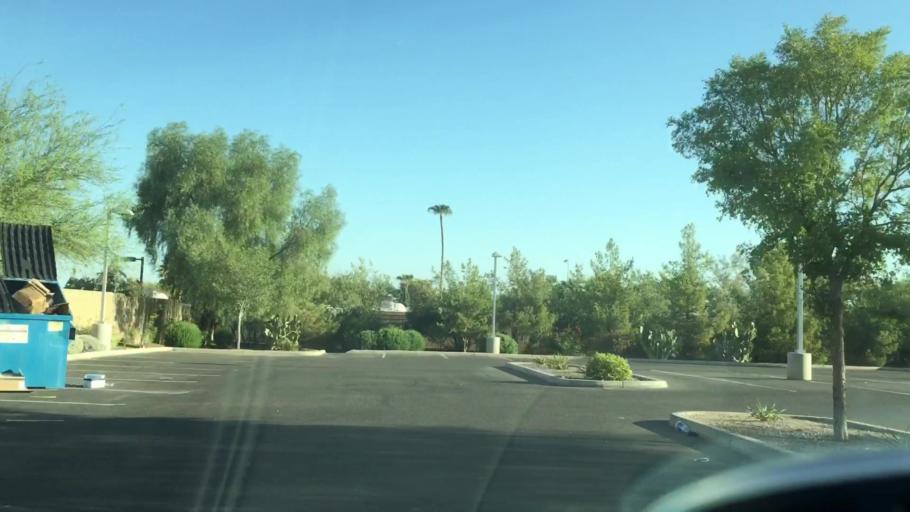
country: US
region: Arizona
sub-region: Maricopa County
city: Guadalupe
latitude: 33.3795
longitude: -111.9762
